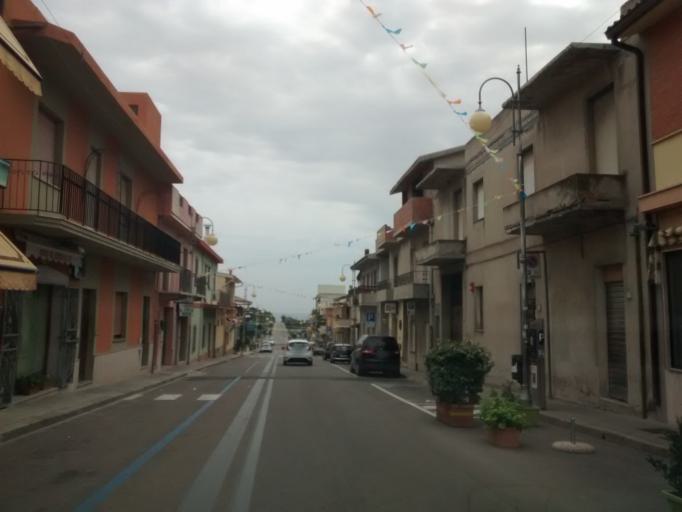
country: IT
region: Sardinia
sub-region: Provincia di Cagliari
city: Villasimius
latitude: 39.1406
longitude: 9.5215
